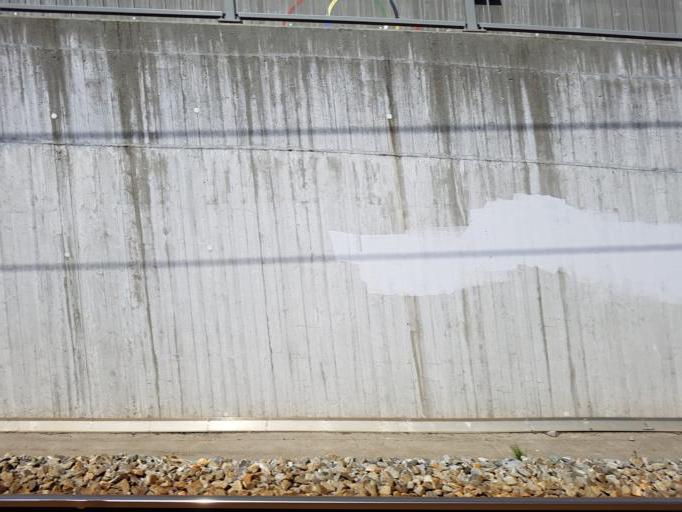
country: NO
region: Hordaland
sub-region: Bergen
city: Ytrebygda
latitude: 60.2967
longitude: 5.2714
